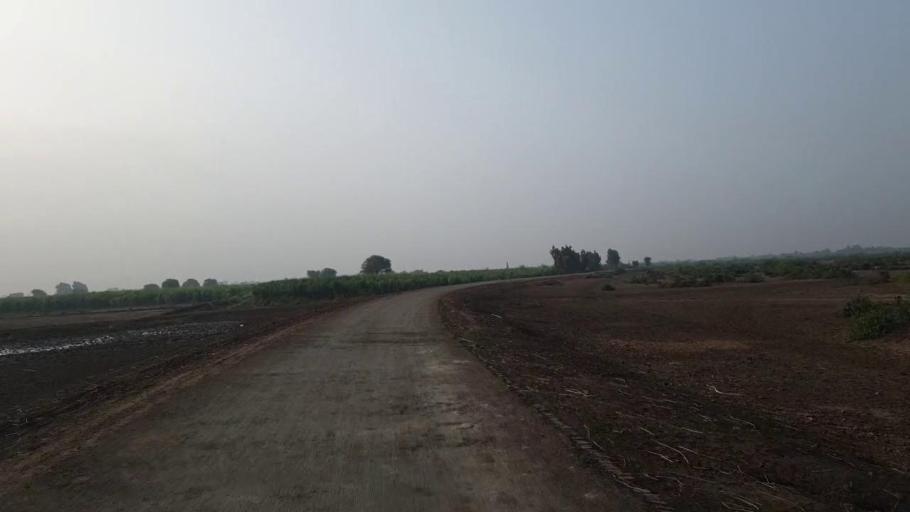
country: PK
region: Sindh
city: Tando Muhammad Khan
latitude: 25.1558
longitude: 68.6097
